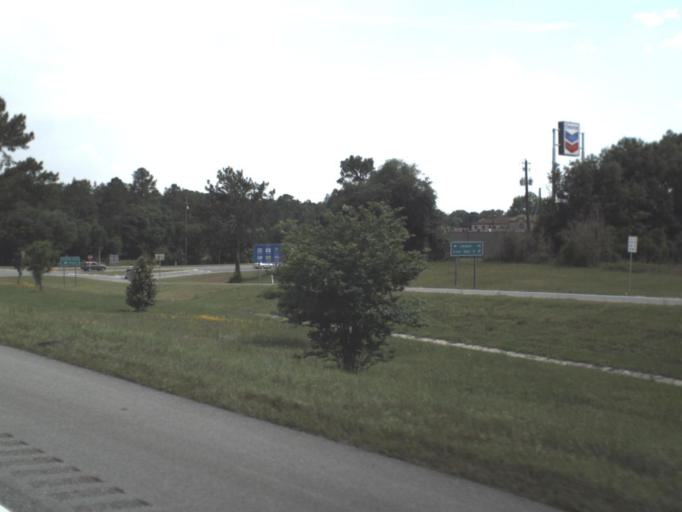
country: US
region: Florida
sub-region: Suwannee County
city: Live Oak
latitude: 30.3315
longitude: -82.9640
